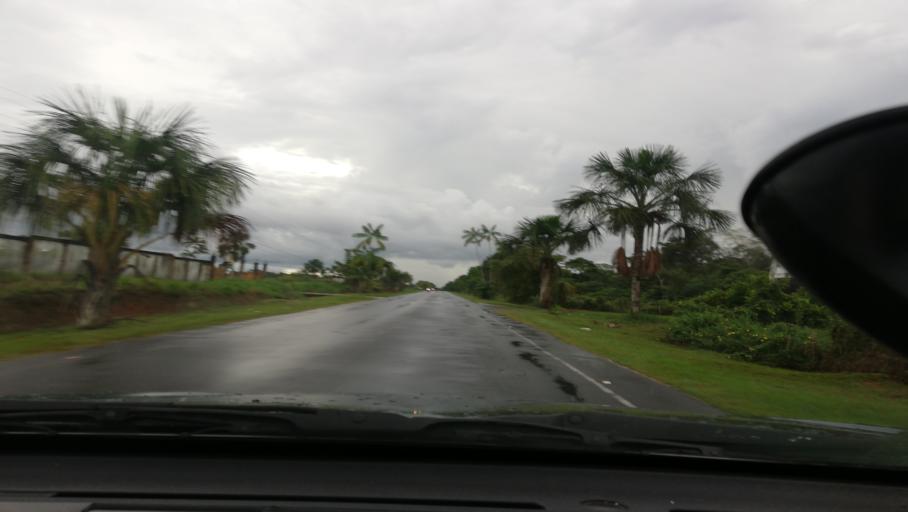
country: PE
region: Loreto
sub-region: Provincia de Maynas
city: Iquitos
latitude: -3.9025
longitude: -73.3543
